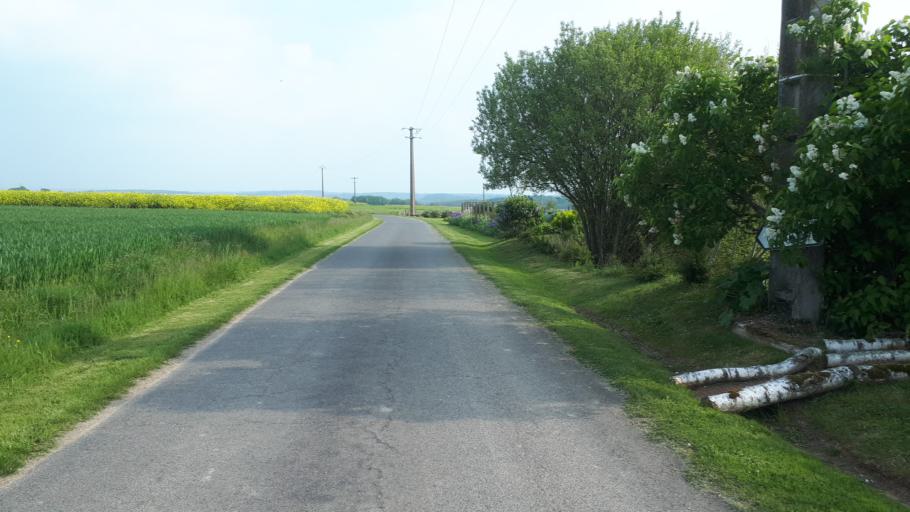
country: FR
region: Centre
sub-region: Departement du Loir-et-Cher
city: Lunay
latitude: 47.8341
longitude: 0.9472
